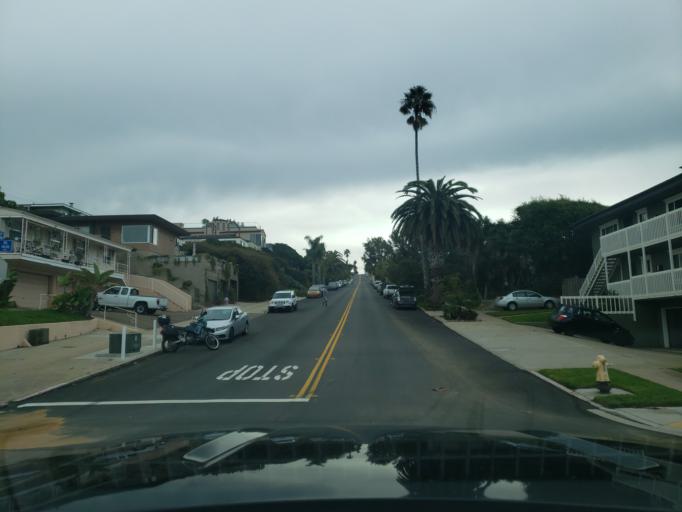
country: US
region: California
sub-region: San Diego County
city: Coronado
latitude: 32.7405
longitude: -117.2513
